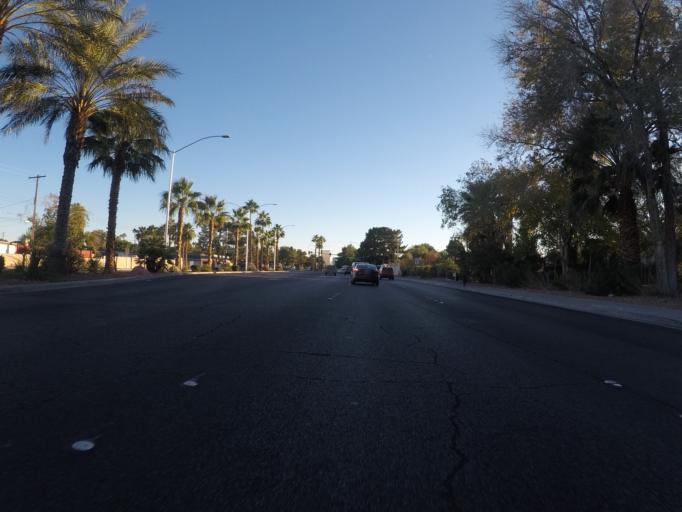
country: US
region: Nevada
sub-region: Clark County
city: Las Vegas
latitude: 36.1673
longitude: -115.1727
